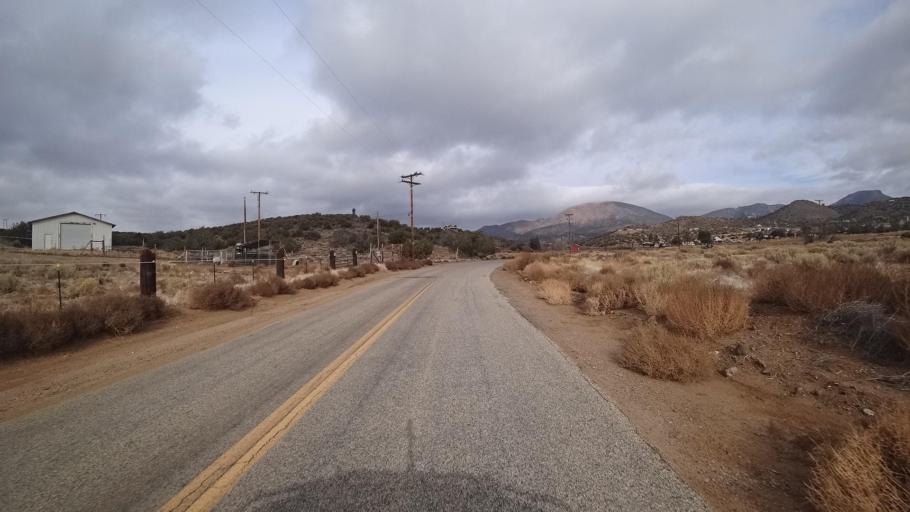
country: US
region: California
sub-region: Kern County
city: Tehachapi
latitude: 35.1764
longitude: -118.3370
